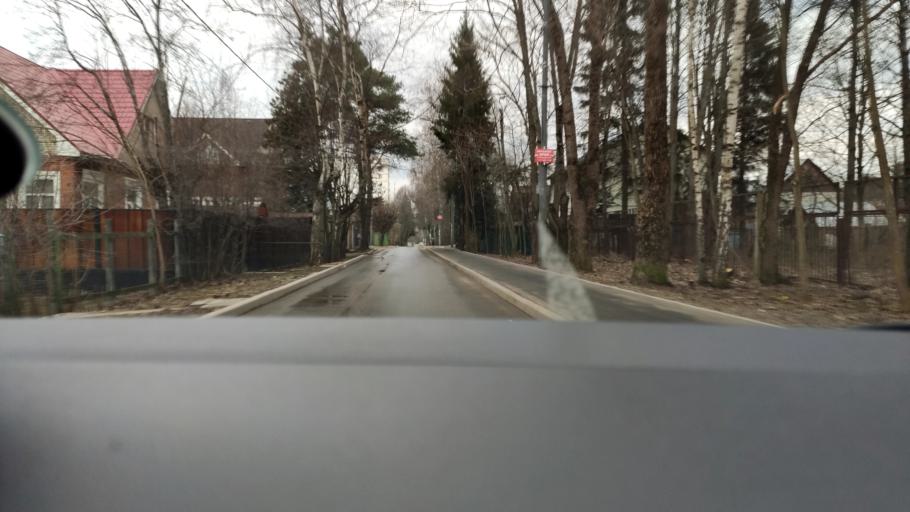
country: RU
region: Moskovskaya
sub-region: Leninskiy Rayon
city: Vnukovo
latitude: 55.6137
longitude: 37.3022
